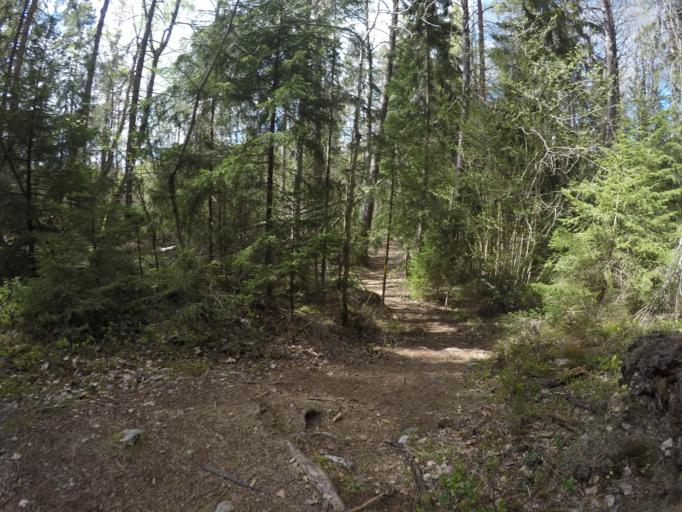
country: SE
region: Soedermanland
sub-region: Eskilstuna Kommun
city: Hallbybrunn
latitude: 59.3553
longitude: 16.3888
